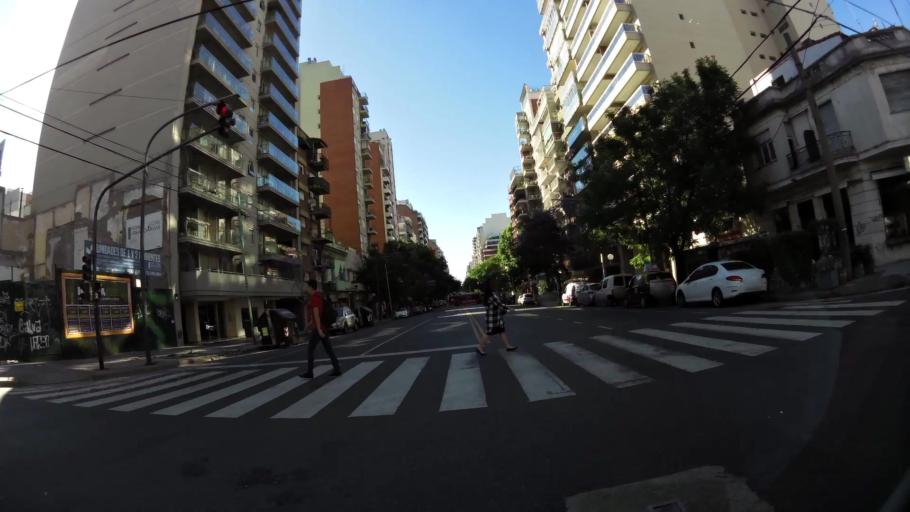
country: AR
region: Buenos Aires F.D.
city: Colegiales
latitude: -34.5611
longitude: -58.4647
